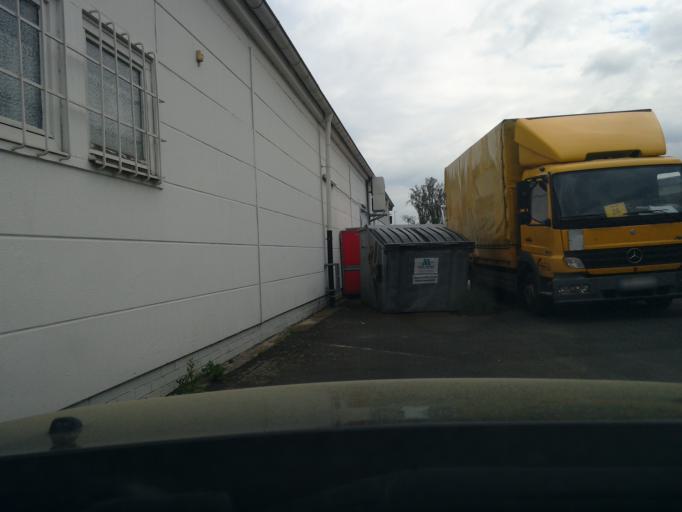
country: DE
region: Hesse
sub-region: Regierungsbezirk Darmstadt
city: Gelnhausen
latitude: 50.1950
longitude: 9.1961
